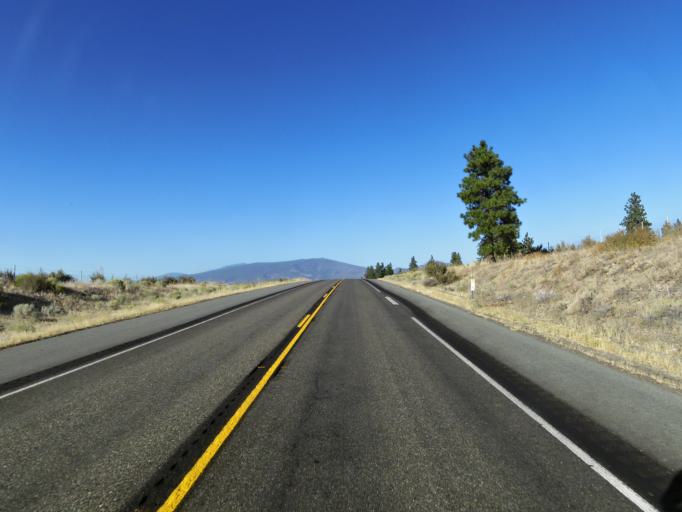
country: US
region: California
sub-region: Siskiyou County
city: Weed
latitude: 41.4912
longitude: -122.3353
